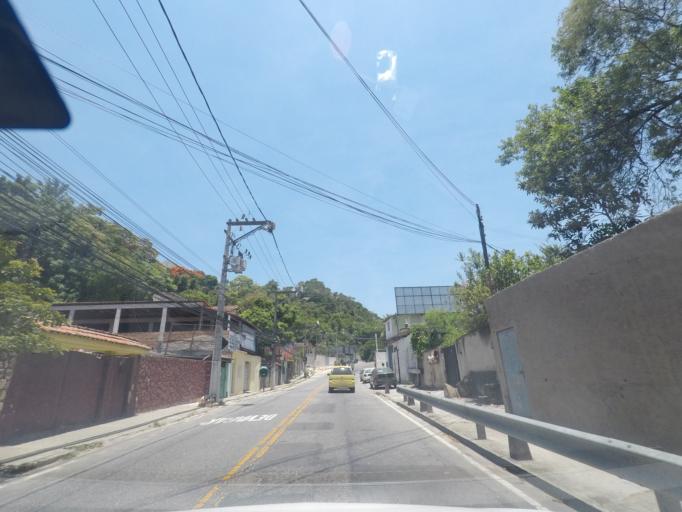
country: BR
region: Rio de Janeiro
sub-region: Niteroi
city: Niteroi
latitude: -22.9104
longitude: -43.0676
